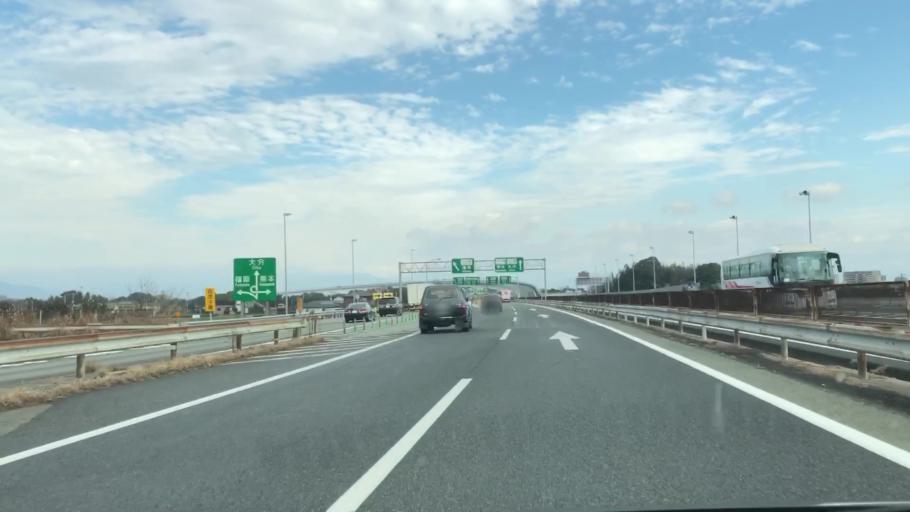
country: JP
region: Saga Prefecture
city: Tosu
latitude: 33.3946
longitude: 130.5321
